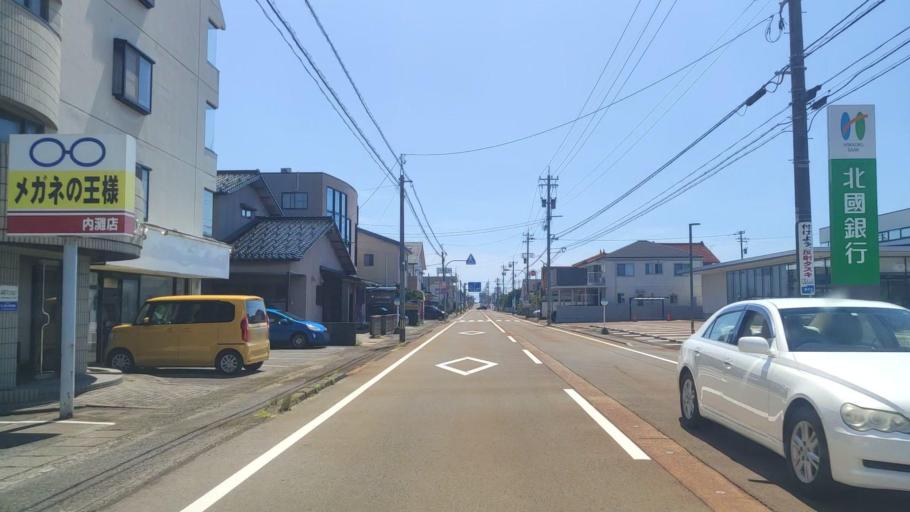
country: JP
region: Ishikawa
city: Kanazawa-shi
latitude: 36.6306
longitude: 136.6333
